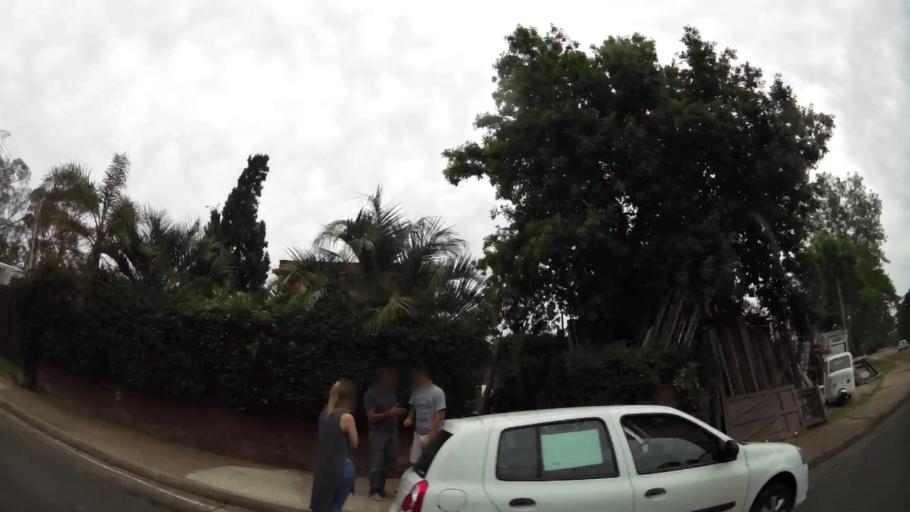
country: UY
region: Maldonado
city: Maldonado
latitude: -34.9115
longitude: -54.9699
